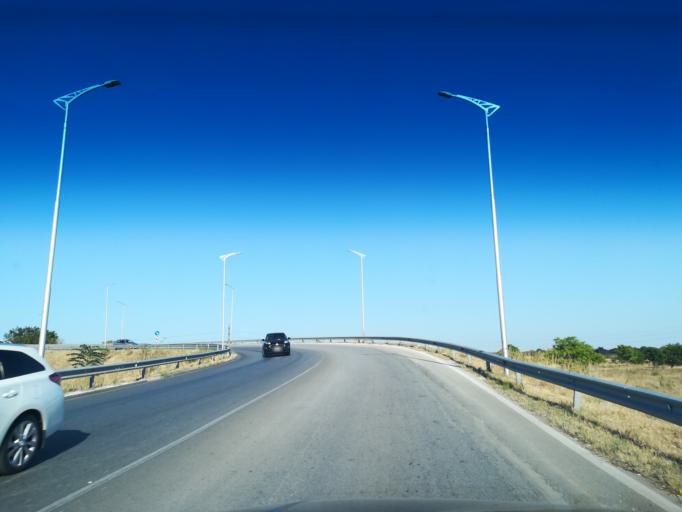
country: BG
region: Plovdiv
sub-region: Obshtina Plovdiv
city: Plovdiv
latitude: 42.1466
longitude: 24.8072
